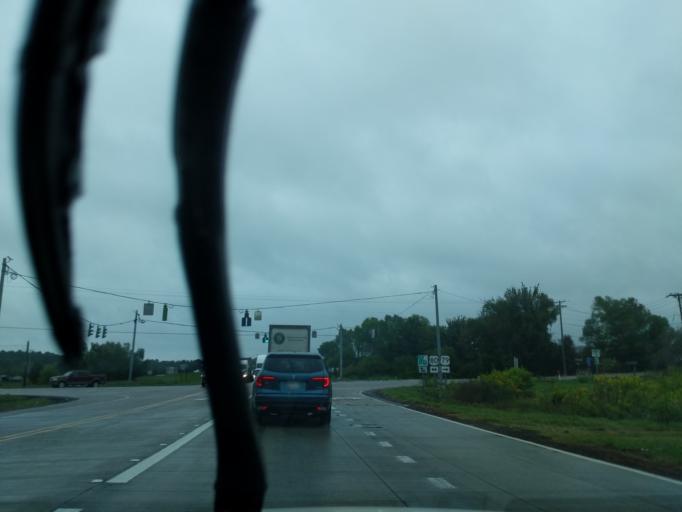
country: US
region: Louisiana
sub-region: Caddo Parish
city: Greenwood
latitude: 32.4429
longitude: -93.9817
